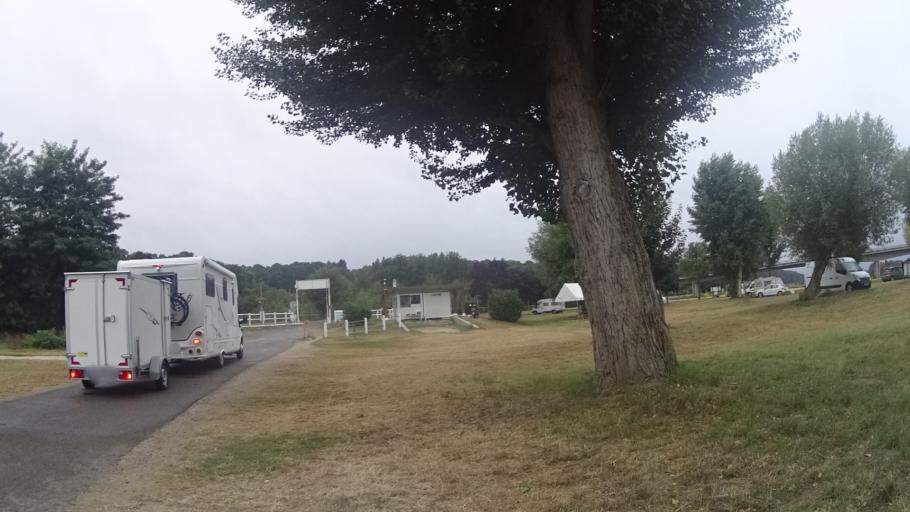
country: FR
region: Centre
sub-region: Departement du Loir-et-Cher
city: Chaumont-sur-Loire
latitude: 47.4853
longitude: 1.1946
